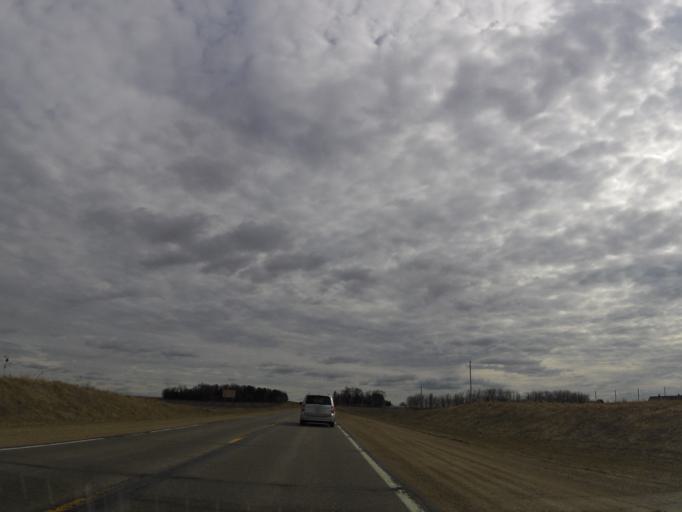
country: US
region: Iowa
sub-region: Chickasaw County
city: New Hampton
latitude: 43.2268
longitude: -92.2986
